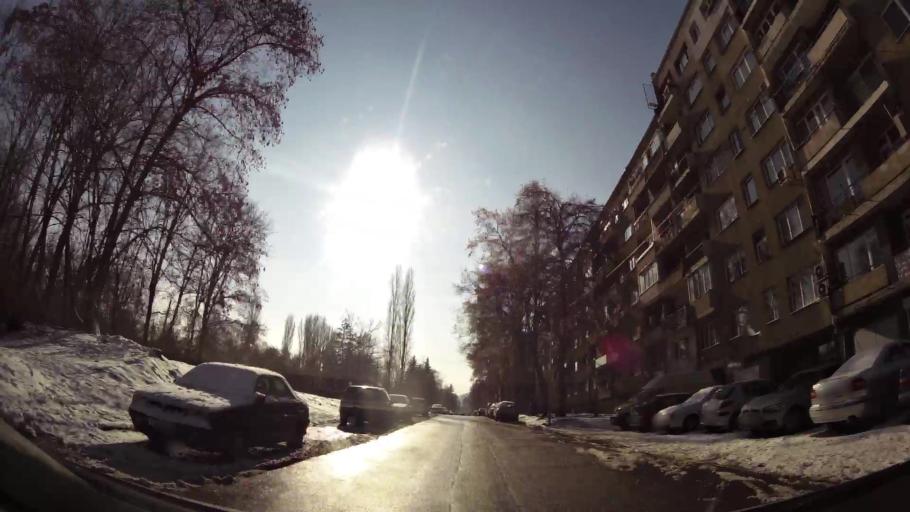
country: BG
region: Sofia-Capital
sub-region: Stolichna Obshtina
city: Sofia
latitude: 42.6780
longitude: 23.3127
